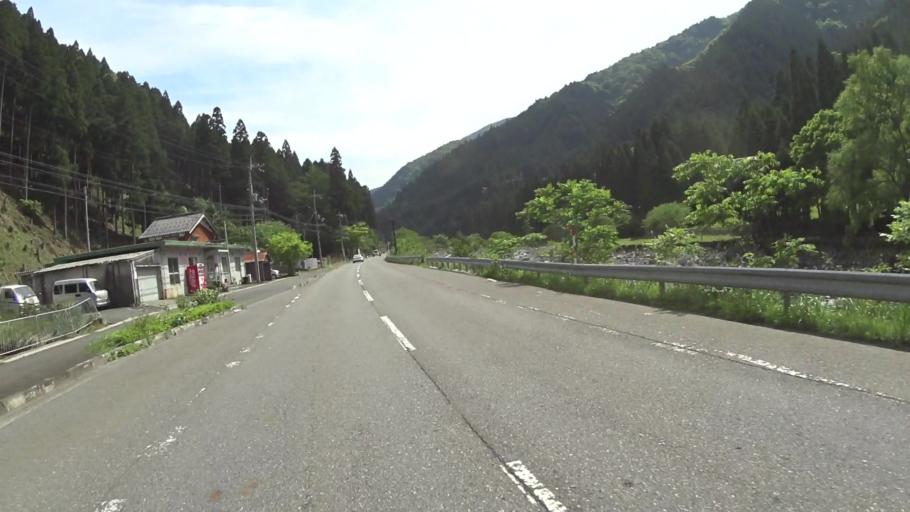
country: JP
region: Shiga Prefecture
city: Kitahama
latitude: 35.2441
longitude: 135.8667
